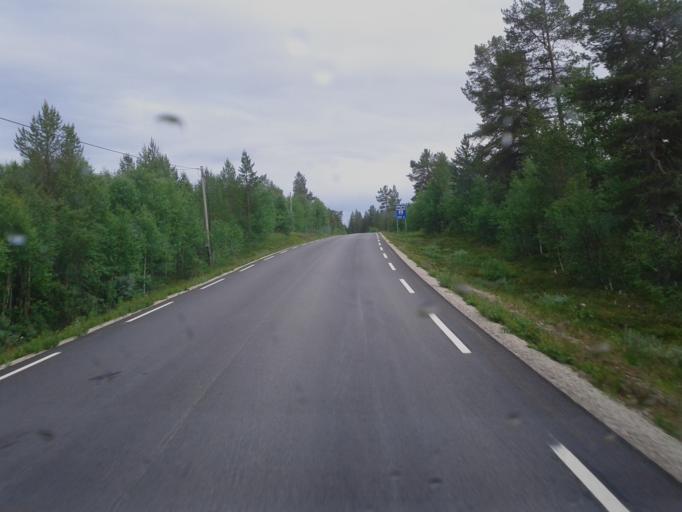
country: NO
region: Hedmark
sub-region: Engerdal
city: Engerdal
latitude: 62.0533
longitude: 11.6867
